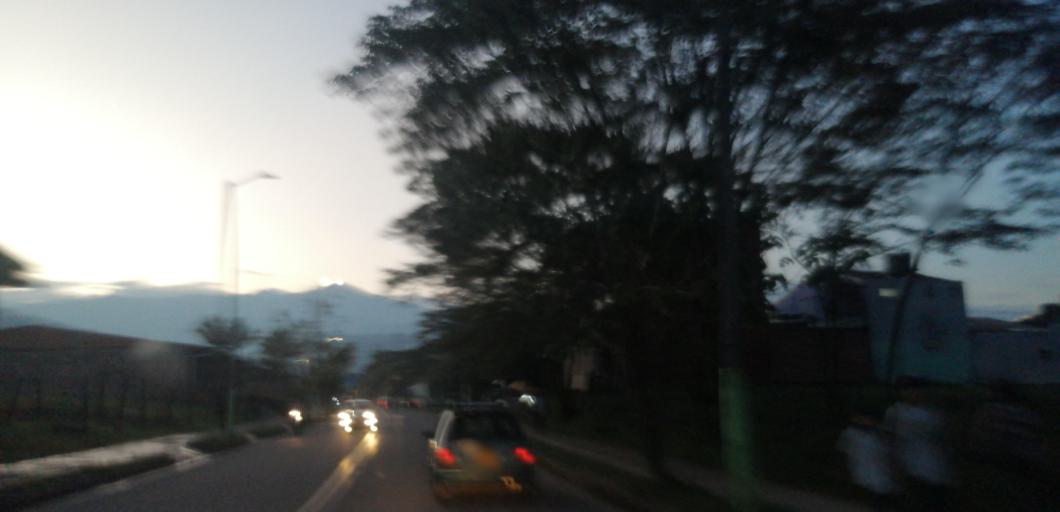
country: CO
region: Meta
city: Acacias
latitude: 3.9903
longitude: -73.7805
